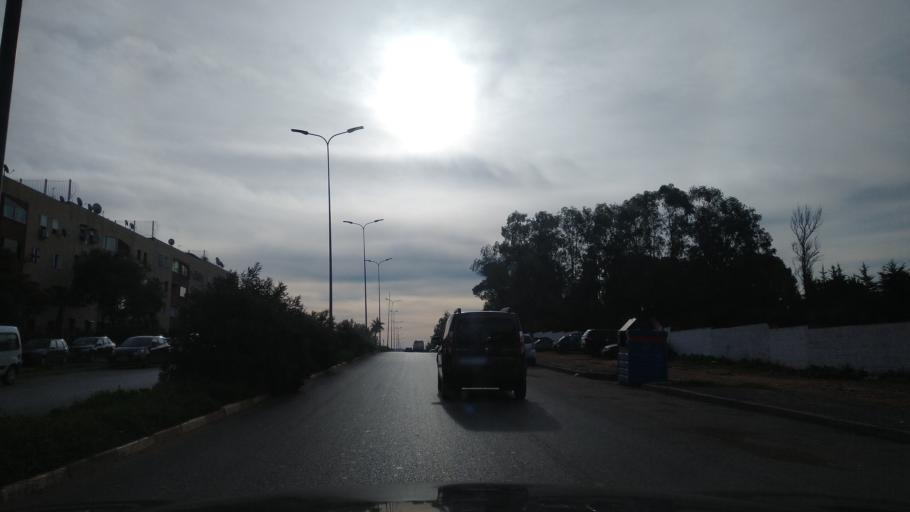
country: MA
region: Rabat-Sale-Zemmour-Zaer
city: Sale
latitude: 33.9983
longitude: -6.7490
